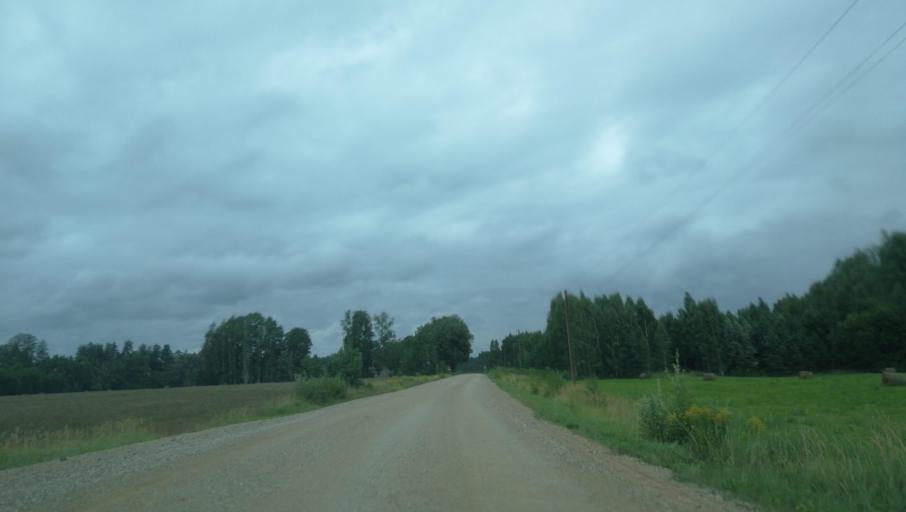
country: LV
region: Beverina
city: Murmuiza
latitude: 57.4123
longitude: 25.5123
